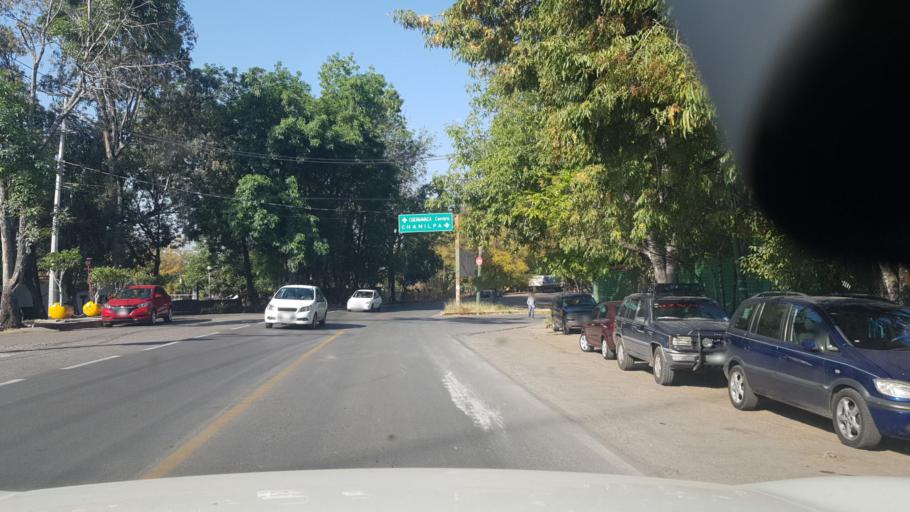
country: MX
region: Morelos
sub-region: Cuernavaca
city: Fraccionamiento Lomas de Ahuatlan
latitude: 18.9666
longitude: -99.2342
